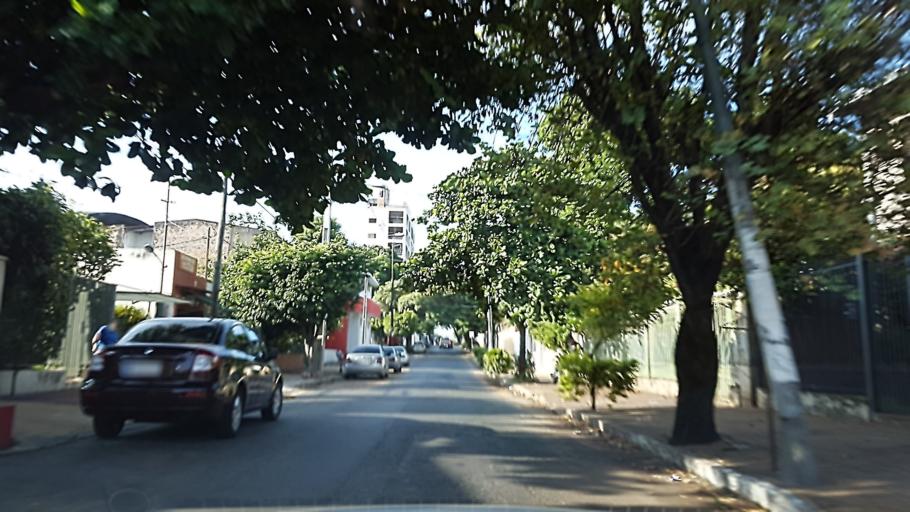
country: PY
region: Asuncion
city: Asuncion
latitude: -25.2841
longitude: -57.6046
